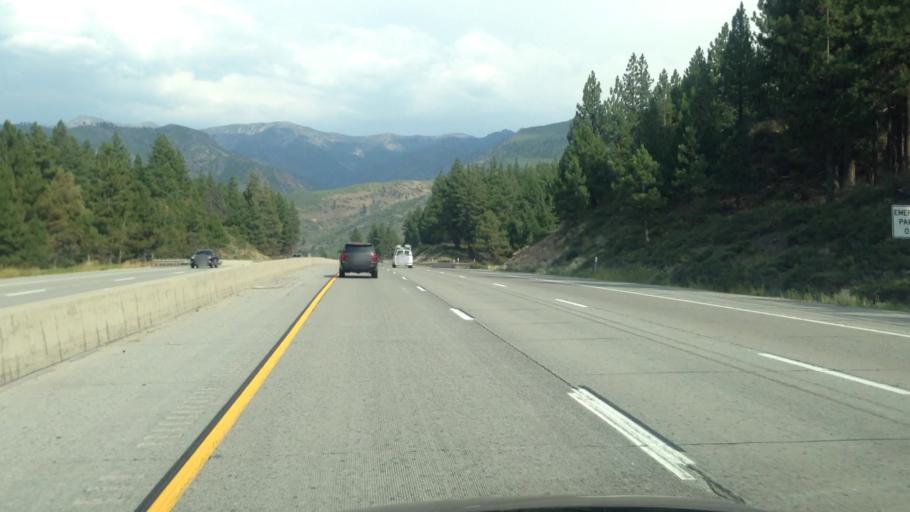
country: US
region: California
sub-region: Nevada County
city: Truckee
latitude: 39.3753
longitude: -120.0685
